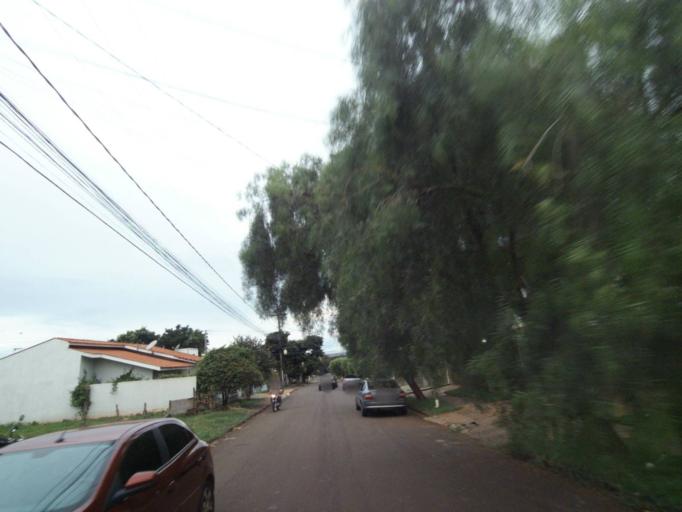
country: BR
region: Parana
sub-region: Campo Mourao
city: Campo Mourao
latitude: -24.0308
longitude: -52.3617
